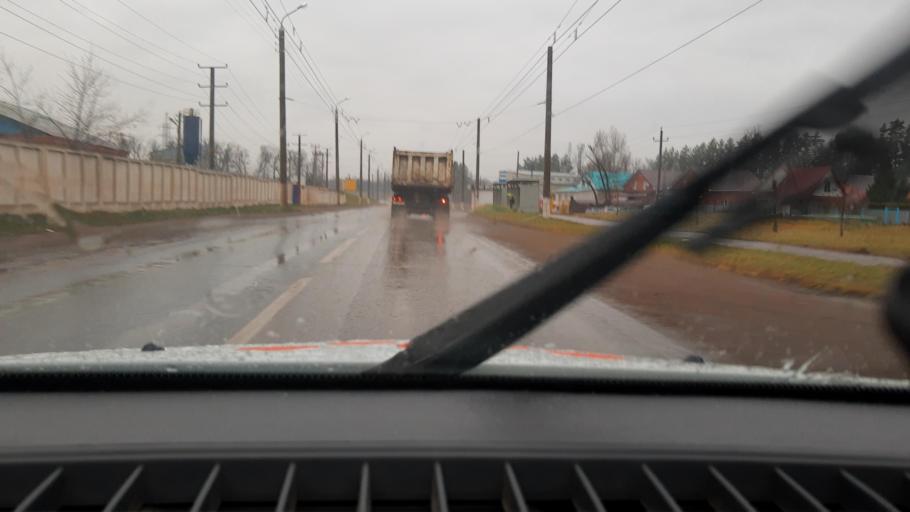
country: RU
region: Bashkortostan
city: Ufa
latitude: 54.7845
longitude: 55.9489
